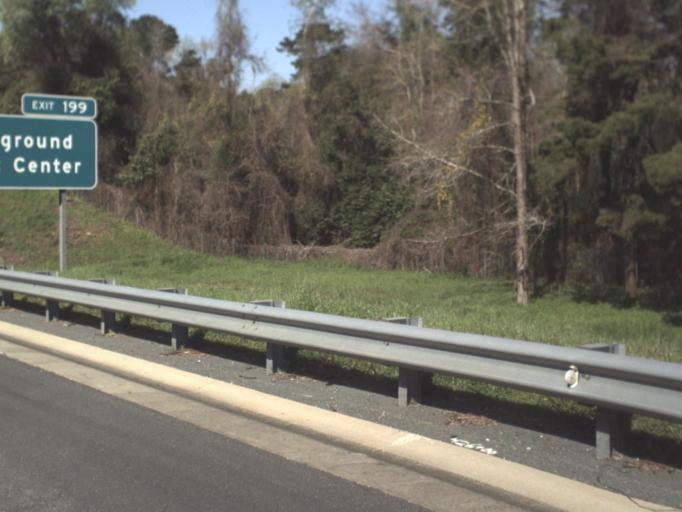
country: US
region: Florida
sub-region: Leon County
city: Tallahassee
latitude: 30.4871
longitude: -84.2943
